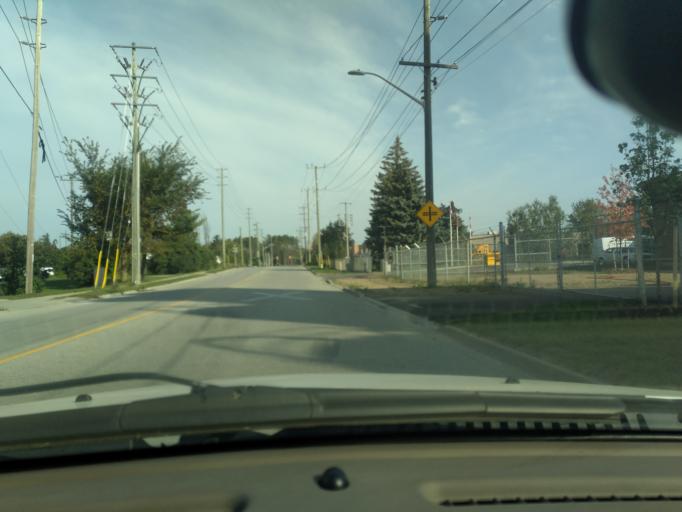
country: CA
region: Ontario
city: Barrie
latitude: 44.3673
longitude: -79.7080
